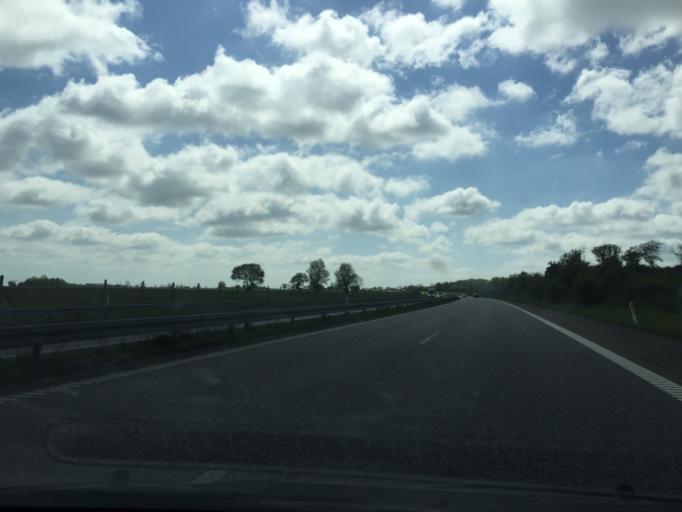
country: DK
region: Zealand
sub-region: Guldborgsund Kommune
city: Sakskobing
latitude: 54.8214
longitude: 11.7062
